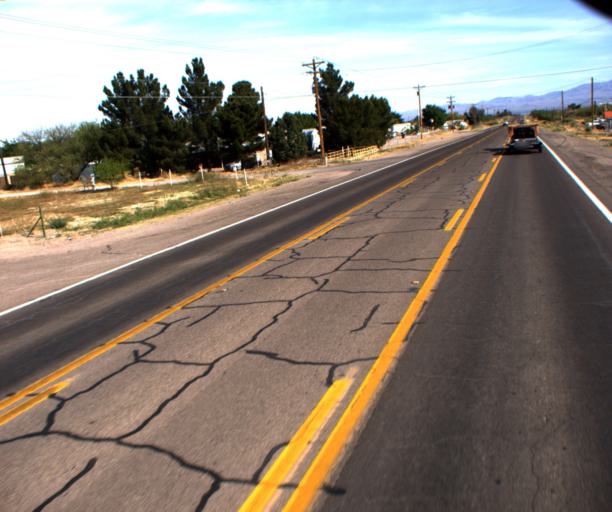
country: US
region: Arizona
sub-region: Graham County
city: Swift Trail Junction
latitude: 32.7411
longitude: -109.7163
